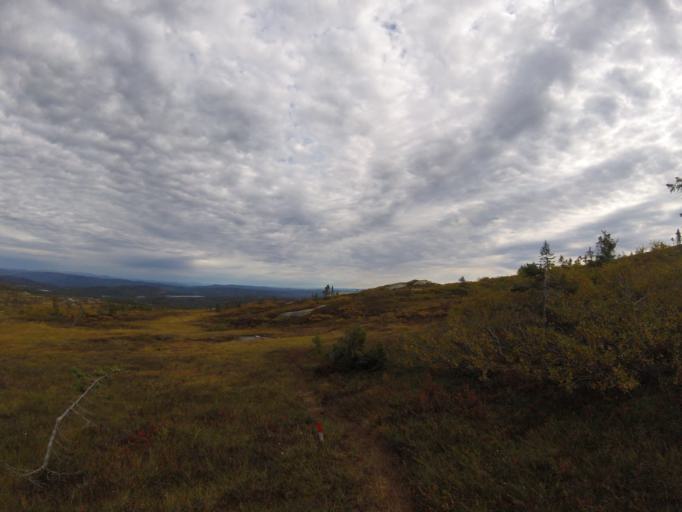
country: NO
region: Buskerud
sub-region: Rollag
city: Rollag
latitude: 59.8071
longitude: 9.3045
